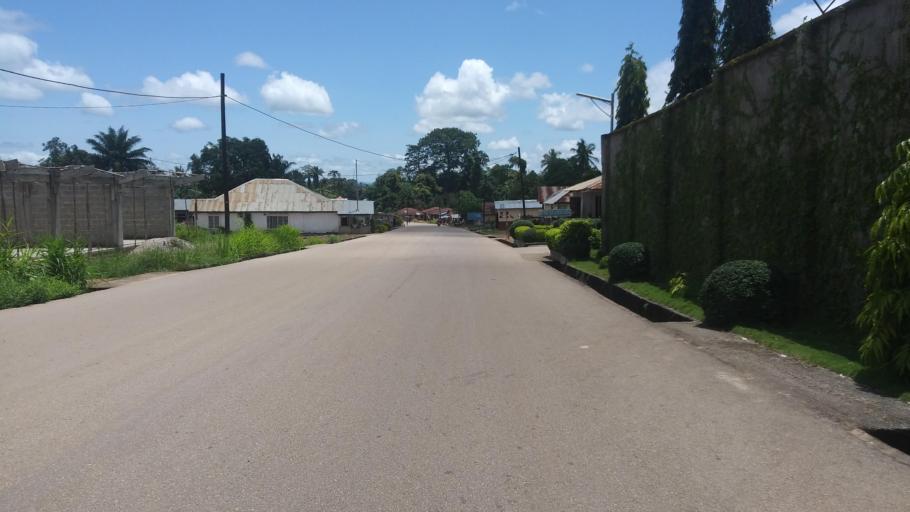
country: SL
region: Northern Province
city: Makeni
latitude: 8.8797
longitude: -12.0252
